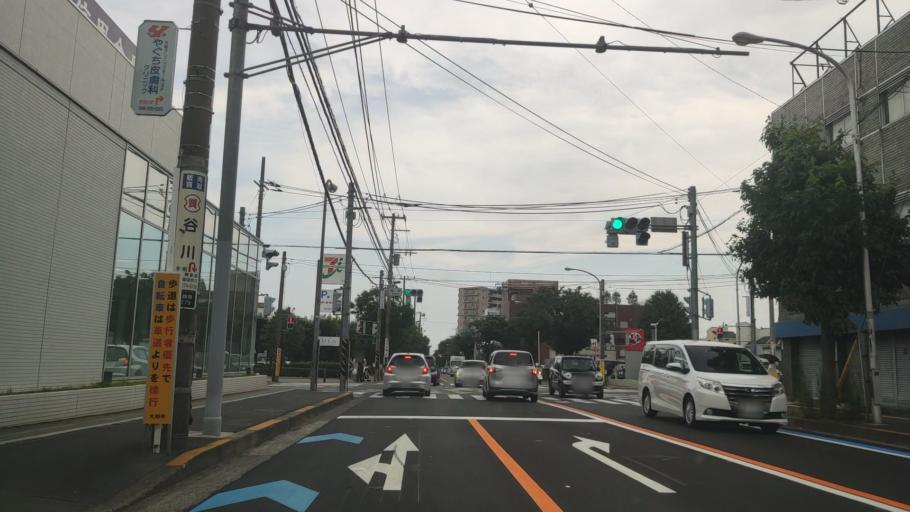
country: JP
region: Kanagawa
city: Minami-rinkan
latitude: 35.4914
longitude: 139.4553
